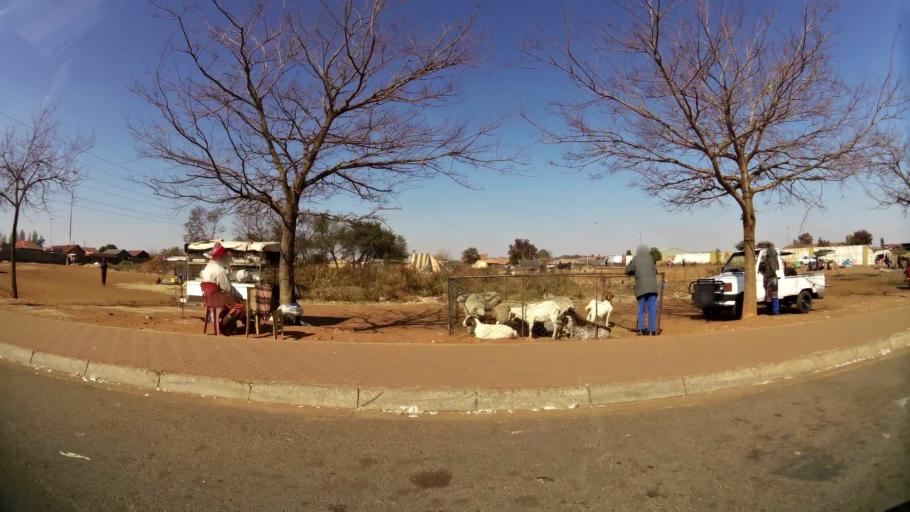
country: ZA
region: Gauteng
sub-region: City of Johannesburg Metropolitan Municipality
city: Soweto
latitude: -26.2864
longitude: 27.8513
